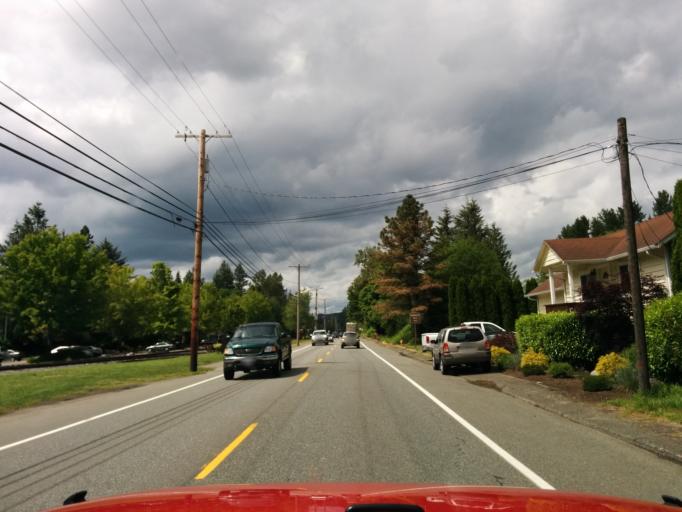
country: US
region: Washington
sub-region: King County
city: Snoqualmie
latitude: 47.5306
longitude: -121.8267
